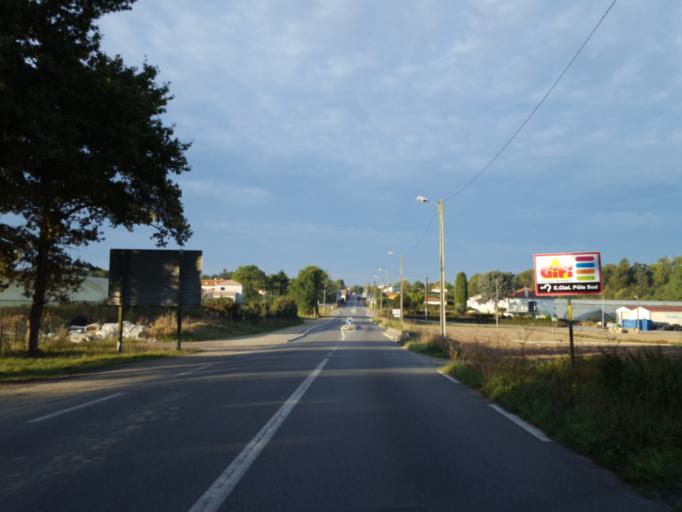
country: FR
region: Pays de la Loire
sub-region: Departement de la Loire-Atlantique
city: Basse-Goulaine
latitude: 47.1969
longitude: -1.4563
